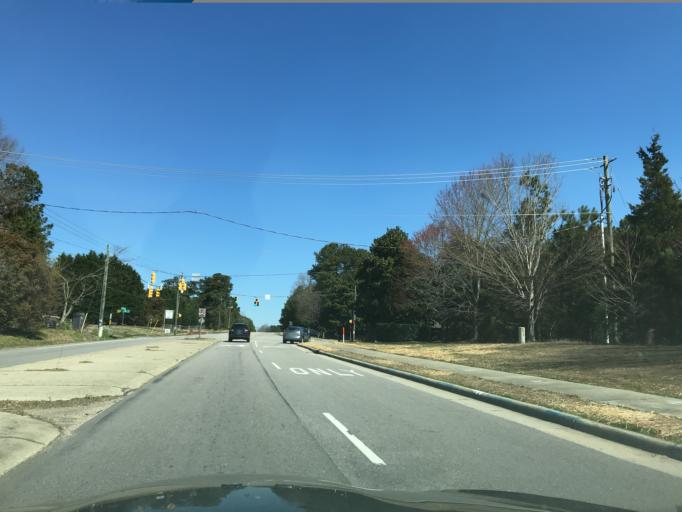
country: US
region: North Carolina
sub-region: Wake County
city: Wake Forest
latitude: 35.9499
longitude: -78.5717
